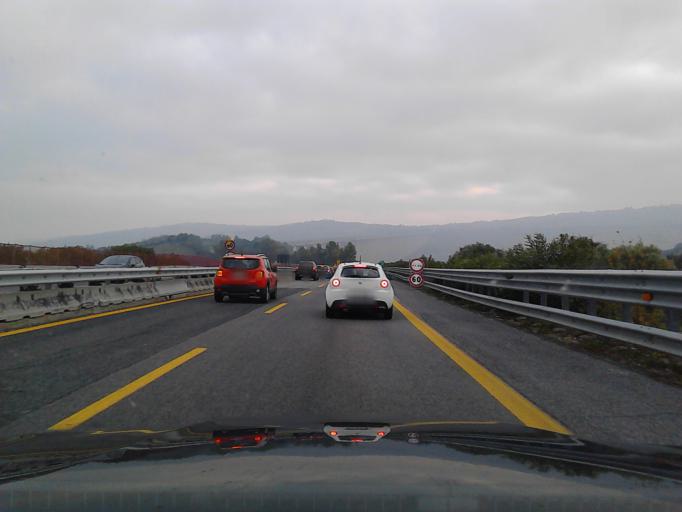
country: IT
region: Abruzzo
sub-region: Provincia di Teramo
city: Tortoreto Lido
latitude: 42.7923
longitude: 13.9340
